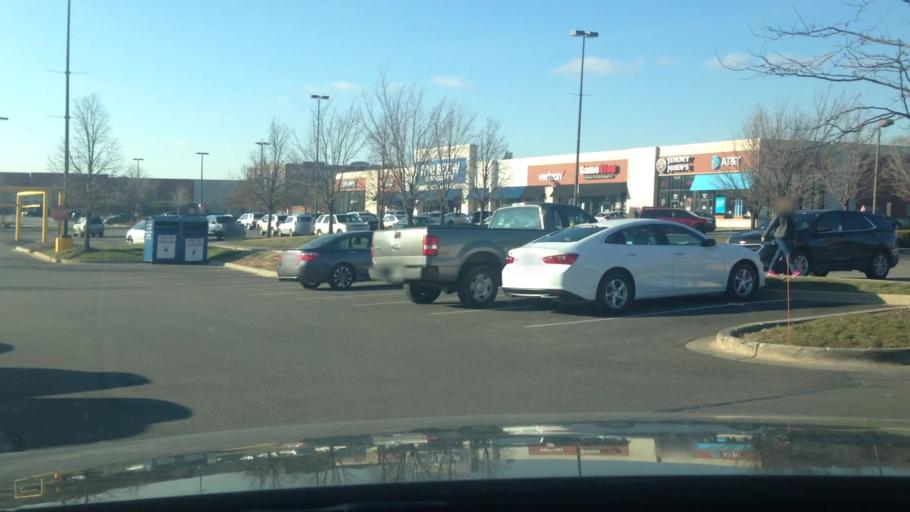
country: US
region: Illinois
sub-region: Cook County
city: Elmwood Park
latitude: 41.9301
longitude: -87.7864
